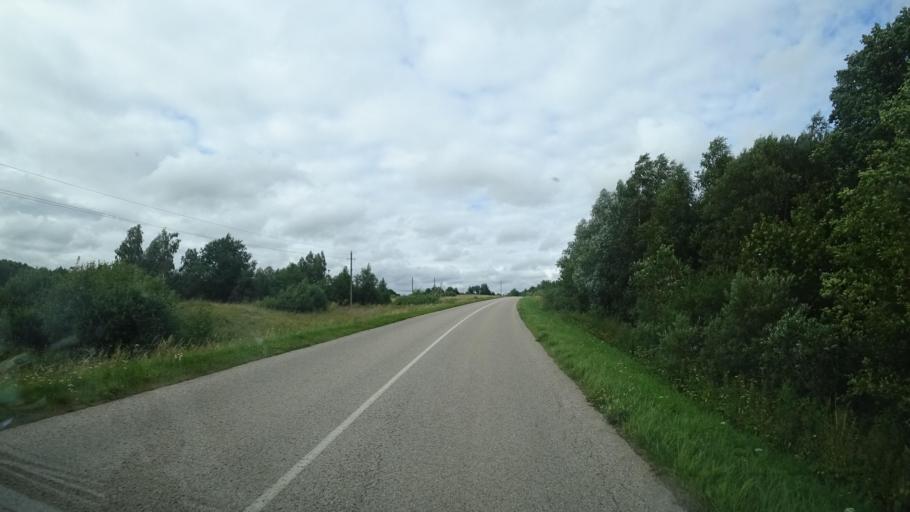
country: LT
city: Virbalis
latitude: 54.4185
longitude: 22.9262
